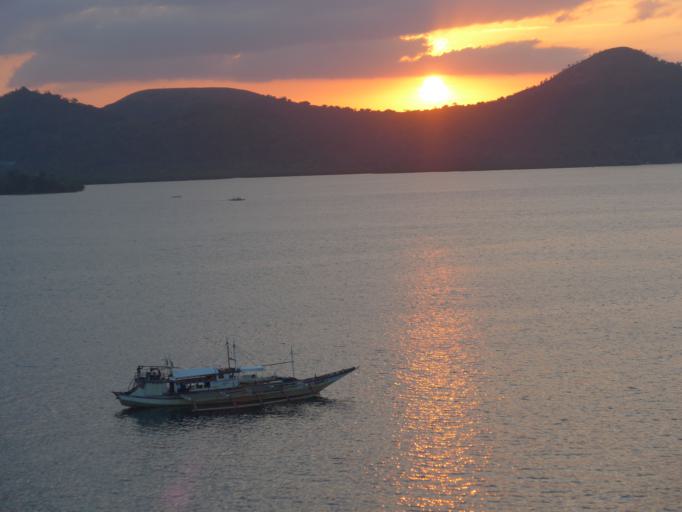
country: PH
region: Mimaropa
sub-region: Province of Palawan
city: Coron
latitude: 11.9904
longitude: 120.2118
